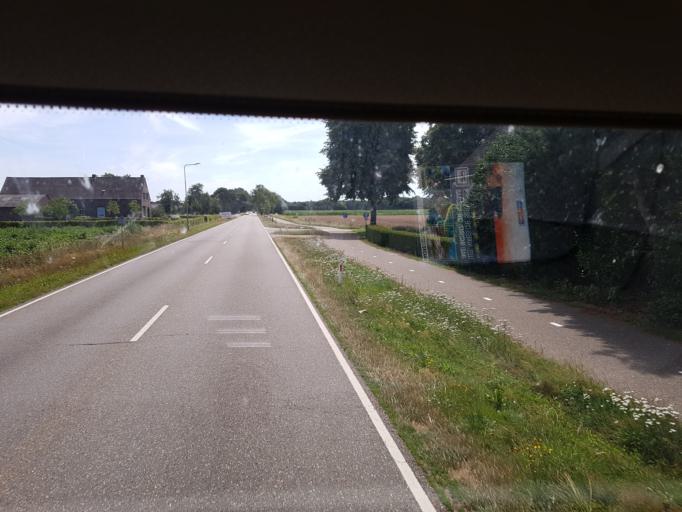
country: NL
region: Limburg
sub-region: Gemeente Leudal
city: Kelpen-Oler
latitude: 51.2535
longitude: 5.8031
